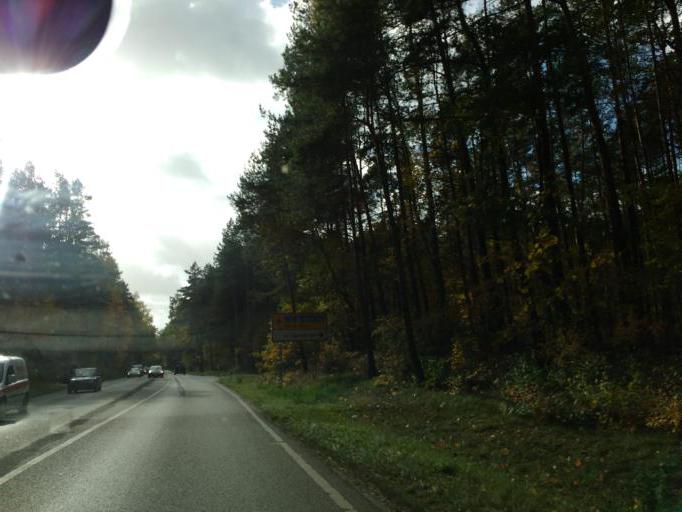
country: DE
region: Brandenburg
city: Petershagen
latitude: 52.5240
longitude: 13.8142
